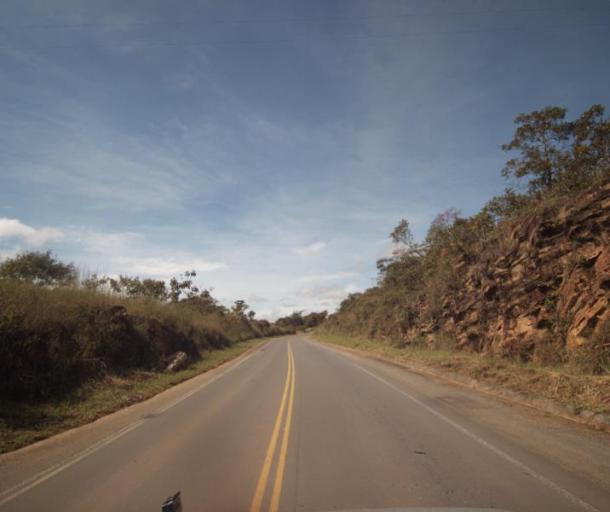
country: BR
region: Goias
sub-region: Abadiania
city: Abadiania
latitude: -16.1415
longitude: -48.8915
